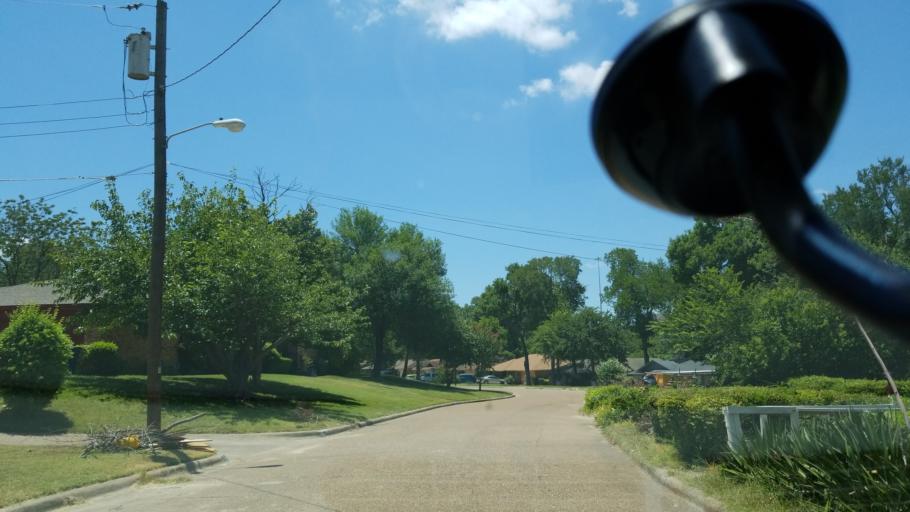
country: US
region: Texas
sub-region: Dallas County
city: Cockrell Hill
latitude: 32.6788
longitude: -96.8201
